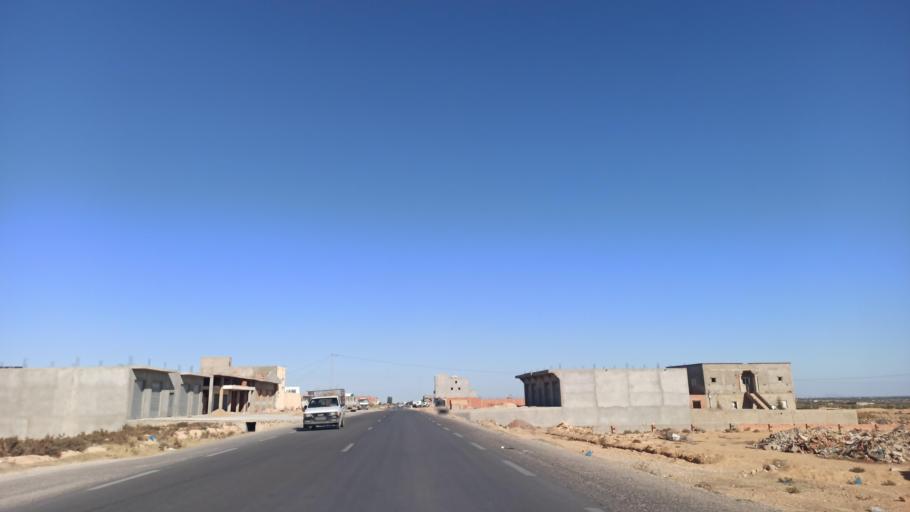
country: TN
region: Sidi Bu Zayd
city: Bi'r al Hufayy
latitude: 34.9469
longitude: 9.2086
